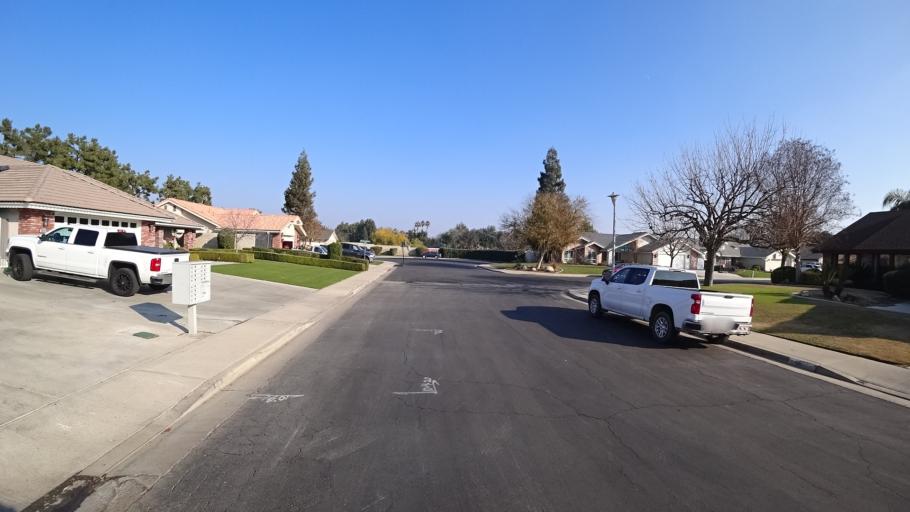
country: US
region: California
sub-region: Kern County
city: Greenacres
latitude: 35.3391
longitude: -119.1085
